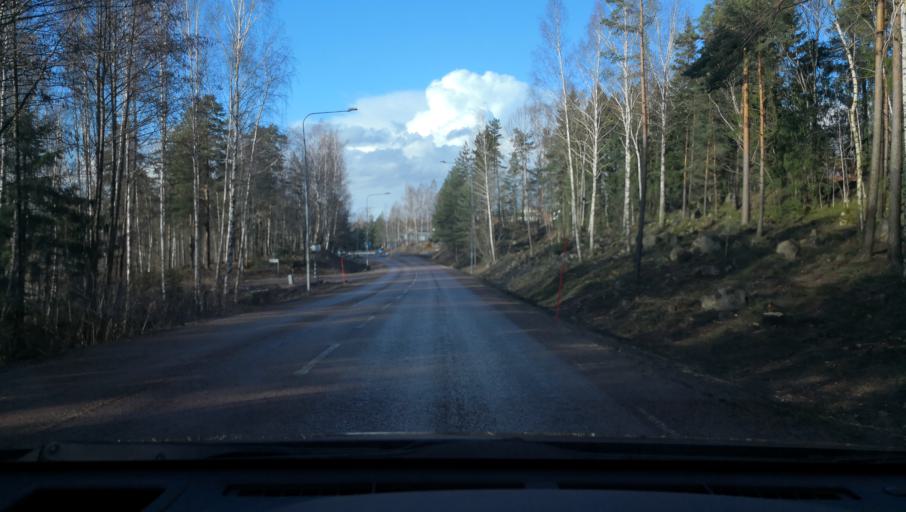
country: SE
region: Vaestmanland
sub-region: Arboga Kommun
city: Arboga
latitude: 59.3831
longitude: 15.8391
